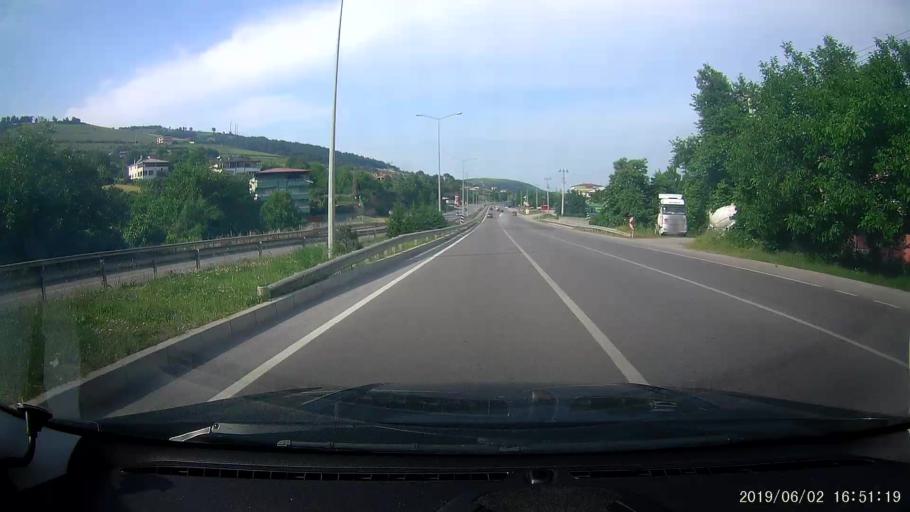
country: TR
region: Samsun
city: Taflan
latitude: 41.2721
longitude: 36.1808
